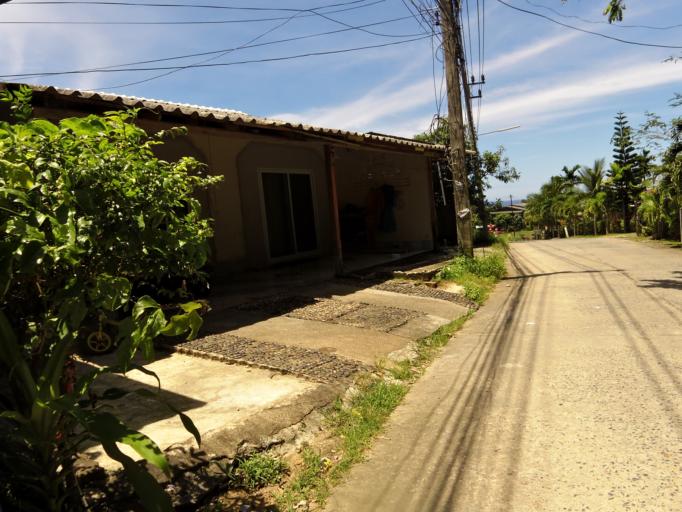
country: TH
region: Phuket
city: Ban Karon
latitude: 7.8499
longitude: 98.3031
